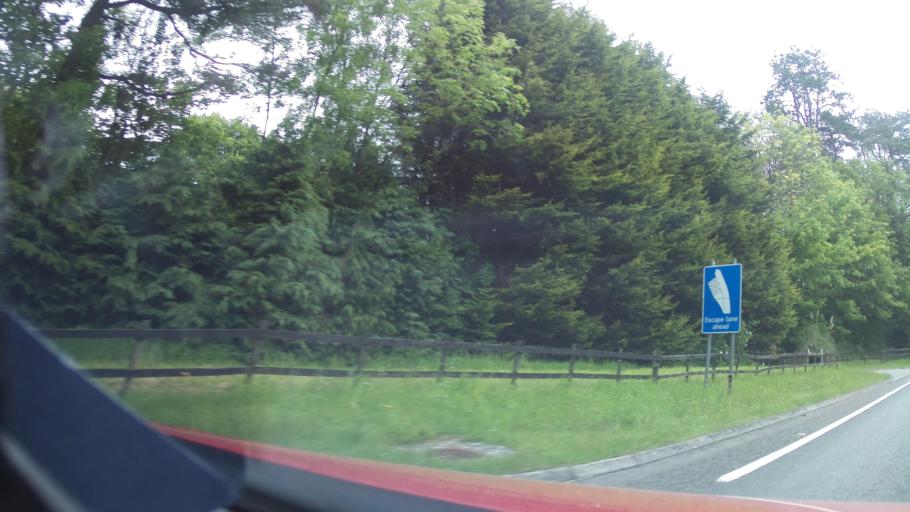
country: GB
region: England
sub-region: Dorset
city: Lyme Regis
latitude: 50.7480
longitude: -2.9231
